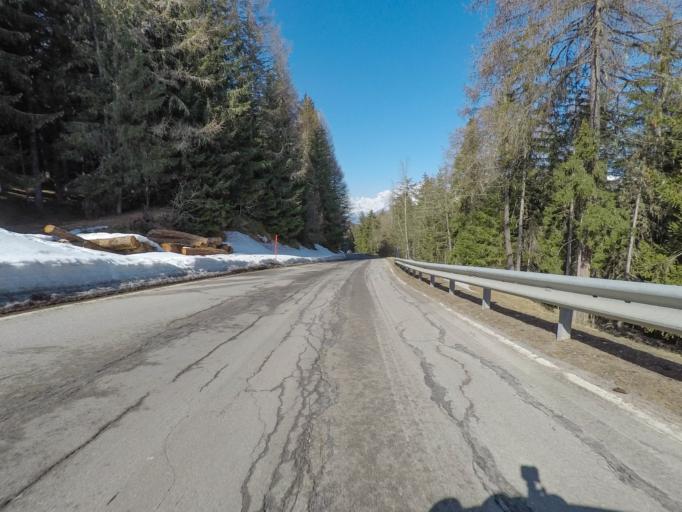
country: CH
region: Valais
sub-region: Herens District
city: Vex
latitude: 46.1992
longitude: 7.3775
